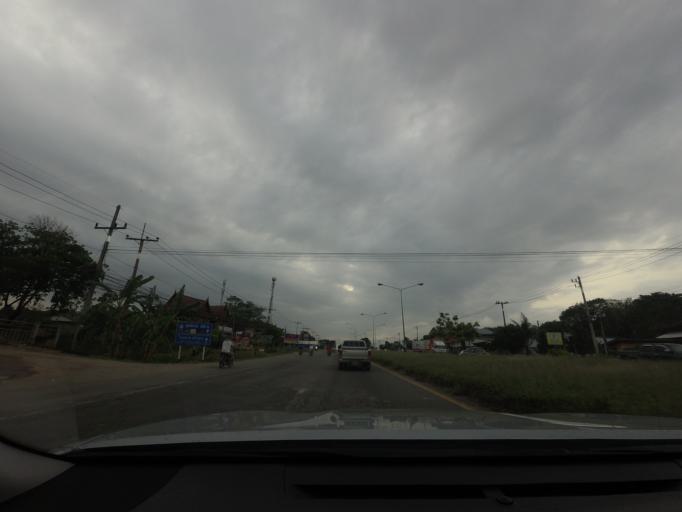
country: TH
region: Surat Thani
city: Phunphin
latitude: 9.0529
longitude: 99.1688
